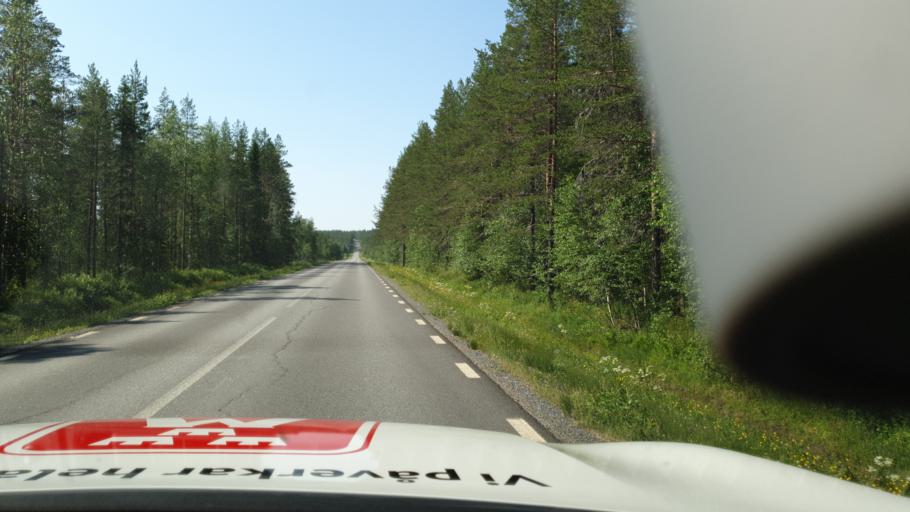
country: SE
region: Vaesterbotten
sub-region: Skelleftea Kommun
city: Langsele
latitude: 64.9842
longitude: 20.0729
